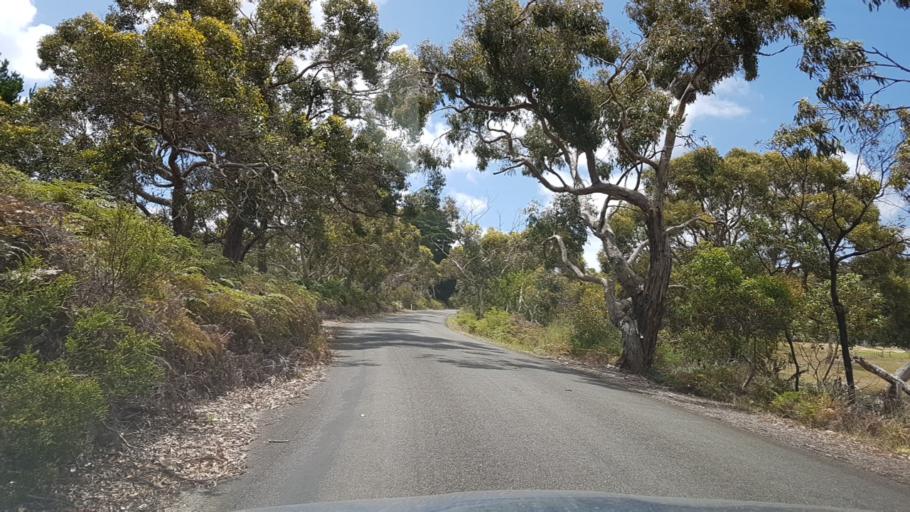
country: AU
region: South Australia
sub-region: Victor Harbor
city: Victor Harbor
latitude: -35.4568
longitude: 138.5925
